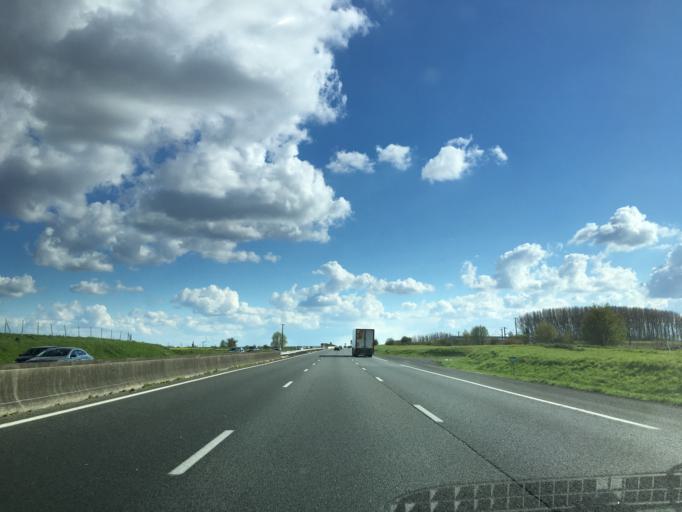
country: FR
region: Nord-Pas-de-Calais
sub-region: Departement du Pas-de-Calais
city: Bapaume
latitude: 50.0974
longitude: 2.8714
